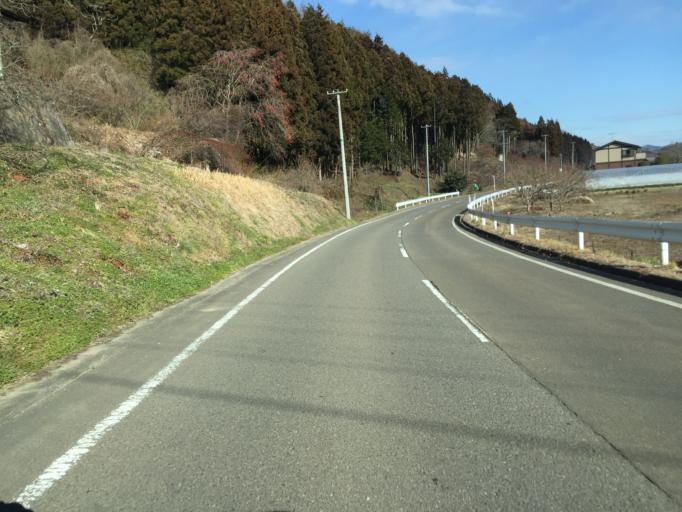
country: JP
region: Fukushima
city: Hobaramachi
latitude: 37.7580
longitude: 140.5698
